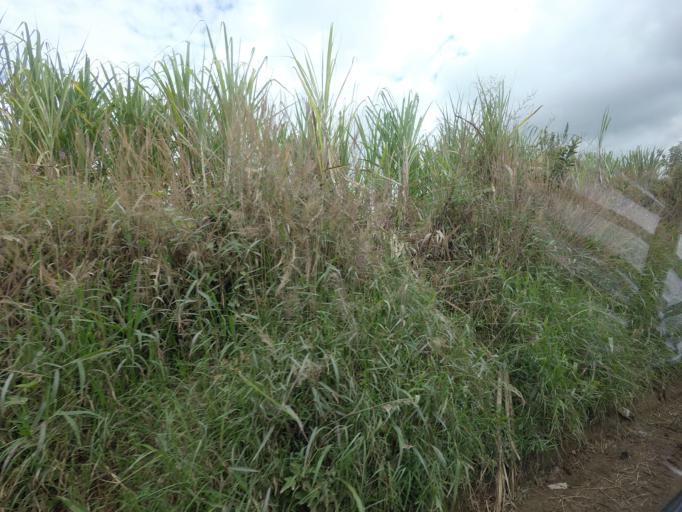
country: CO
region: Huila
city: Isnos
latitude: 1.9562
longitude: -76.2915
